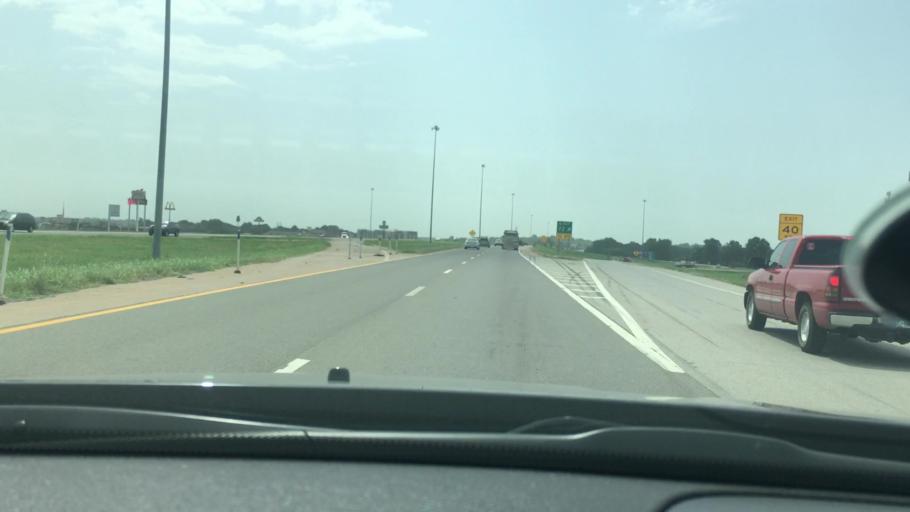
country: US
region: Oklahoma
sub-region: Garvin County
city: Pauls Valley
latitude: 34.7429
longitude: -97.2666
